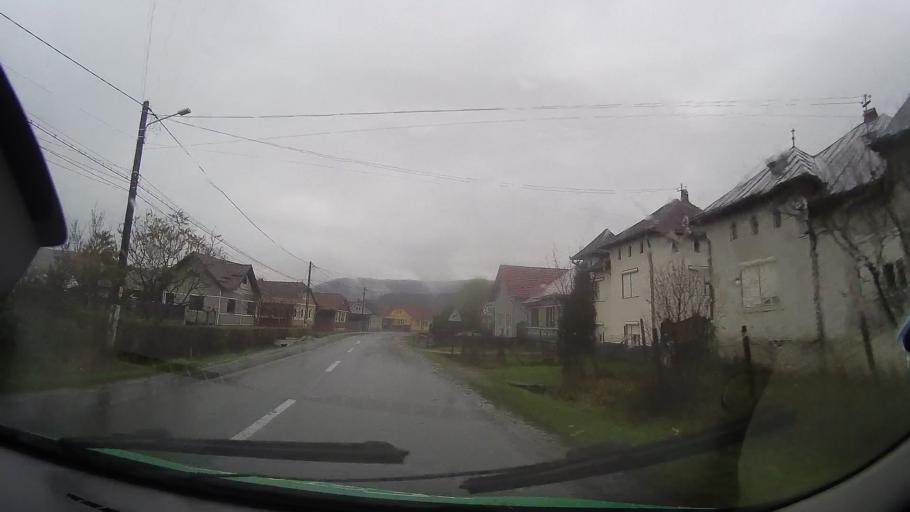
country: RO
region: Bistrita-Nasaud
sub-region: Comuna Mariselu
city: Mariselu
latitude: 47.0130
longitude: 24.5552
